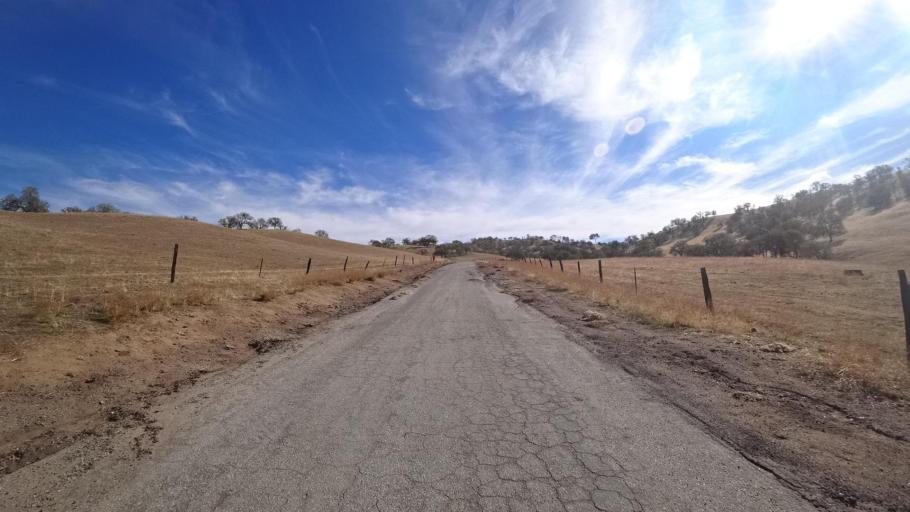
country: US
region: California
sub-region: Kern County
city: Oildale
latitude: 35.5725
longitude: -118.8031
